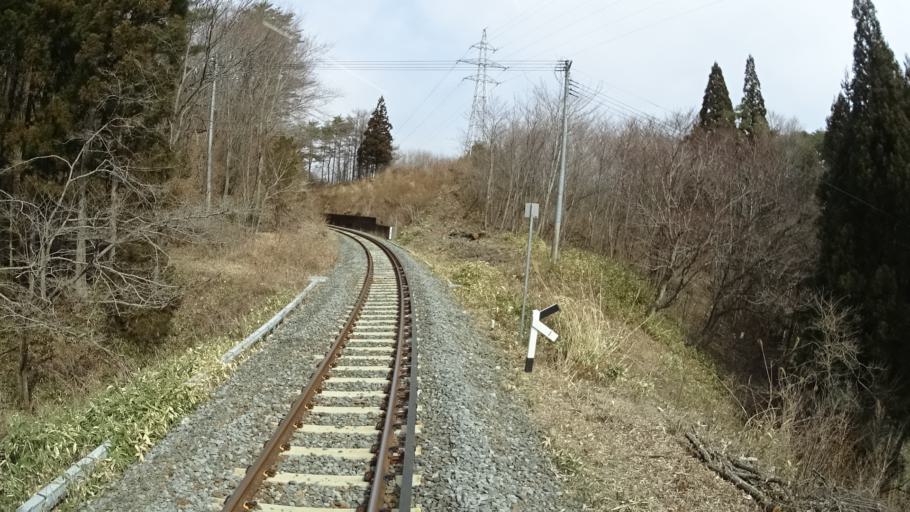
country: JP
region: Iwate
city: Yamada
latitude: 39.4995
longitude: 141.9297
